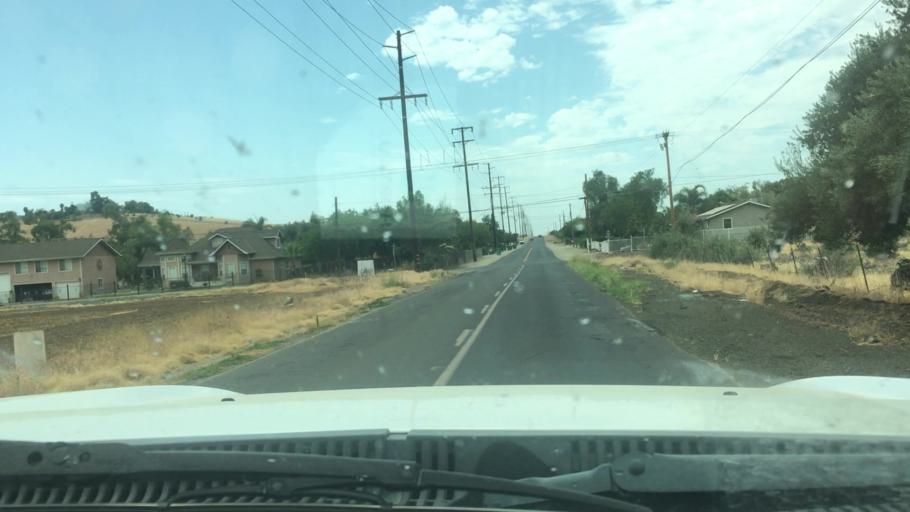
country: US
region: California
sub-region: Tulare County
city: Porterville
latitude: 36.0964
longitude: -119.0170
